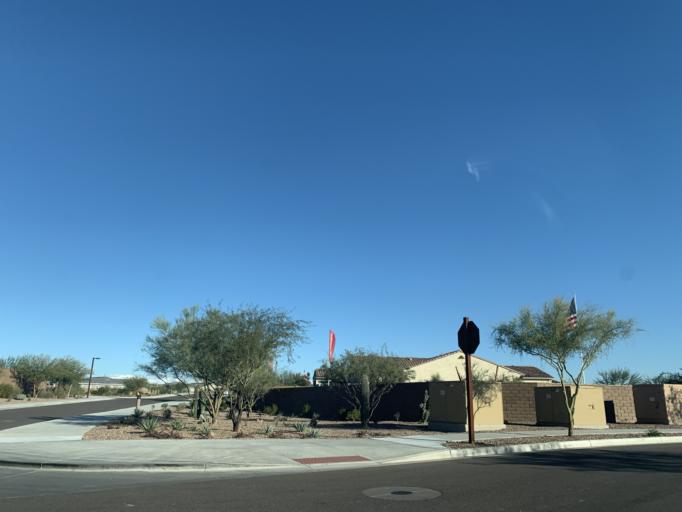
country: US
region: Arizona
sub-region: Maricopa County
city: Cave Creek
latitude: 33.6911
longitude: -112.0154
